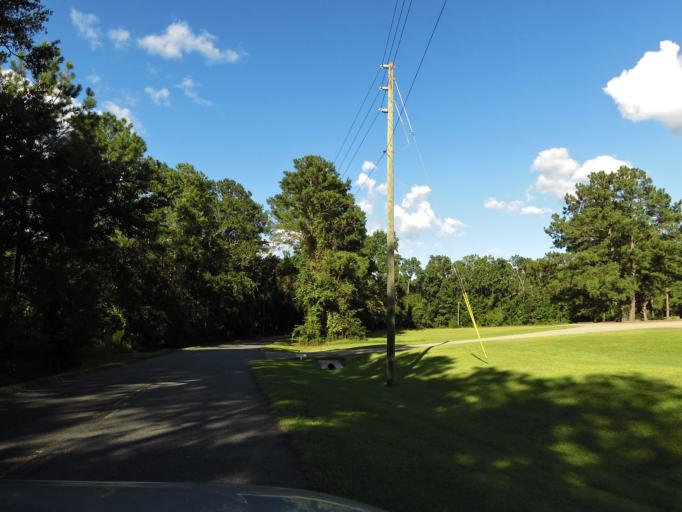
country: US
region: Florida
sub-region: Wakulla County
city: Crawfordville
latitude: 30.0683
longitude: -84.5128
